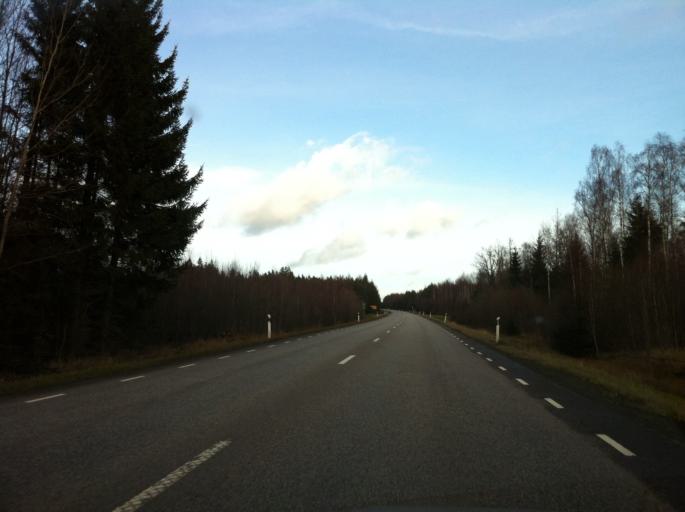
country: SE
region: Kronoberg
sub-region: Almhults Kommun
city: AElmhult
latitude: 56.5869
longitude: 14.1923
